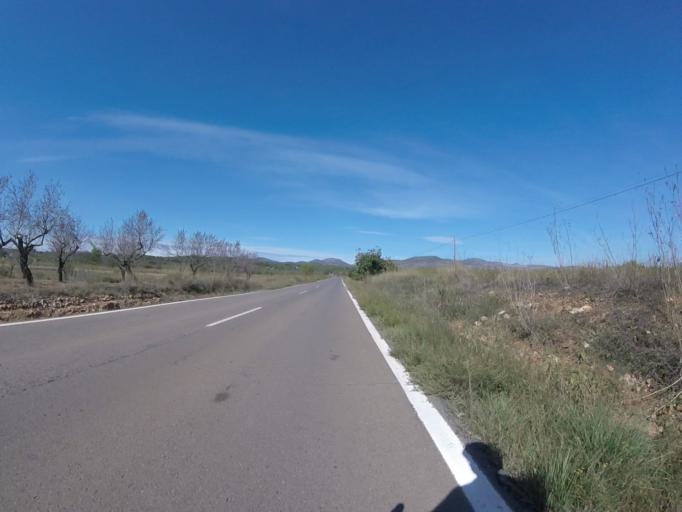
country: ES
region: Valencia
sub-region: Provincia de Castello
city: Benlloch
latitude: 40.2160
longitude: 0.0192
